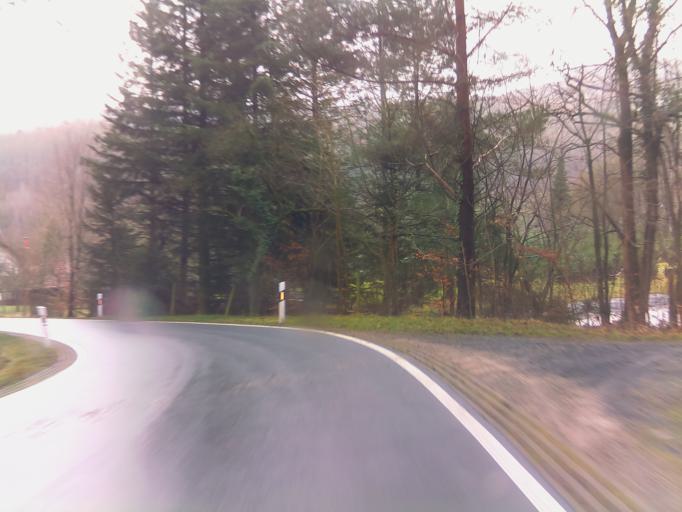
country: DE
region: Hesse
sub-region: Regierungsbezirk Kassel
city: Hofbieber
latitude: 50.5742
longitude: 9.8557
